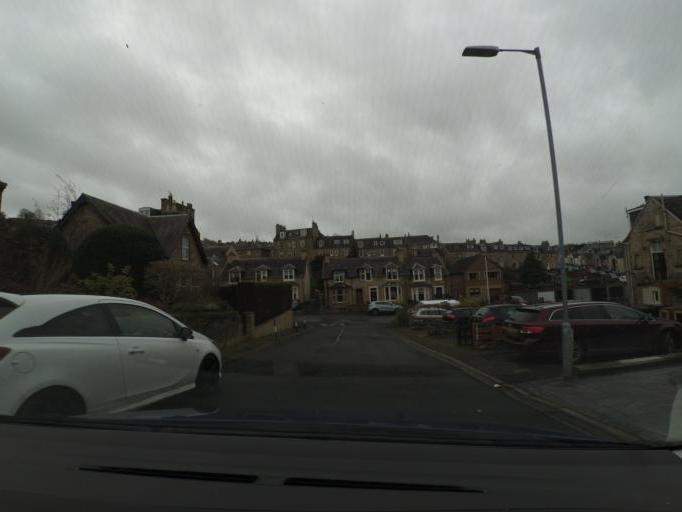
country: GB
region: Scotland
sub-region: The Scottish Borders
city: Hawick
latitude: 55.4223
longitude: -2.7813
